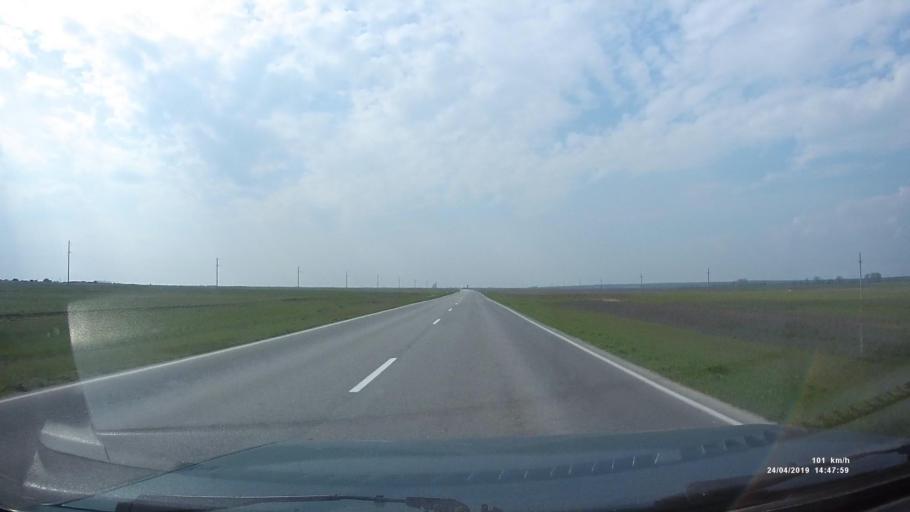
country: RU
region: Rostov
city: Remontnoye
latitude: 46.4966
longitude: 43.7636
